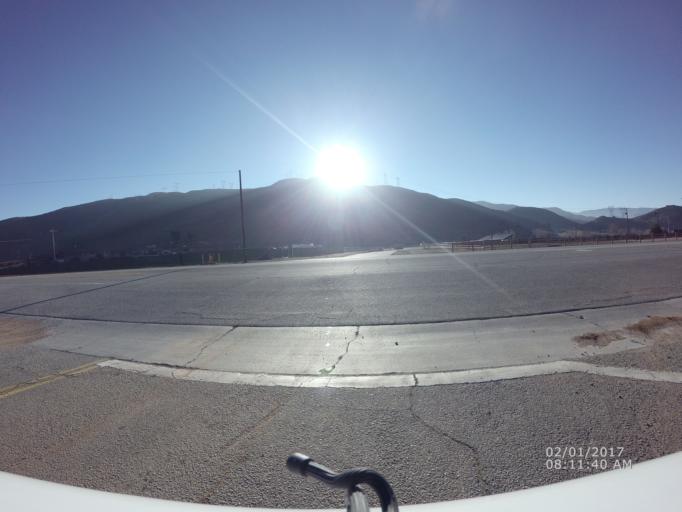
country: US
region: California
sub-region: Los Angeles County
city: Vincent
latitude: 34.5015
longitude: -118.1180
